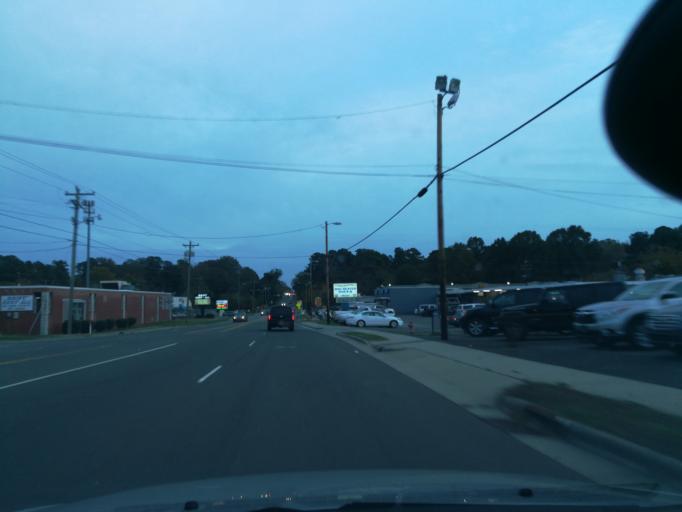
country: US
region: North Carolina
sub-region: Durham County
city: Durham
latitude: 36.0272
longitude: -78.9236
